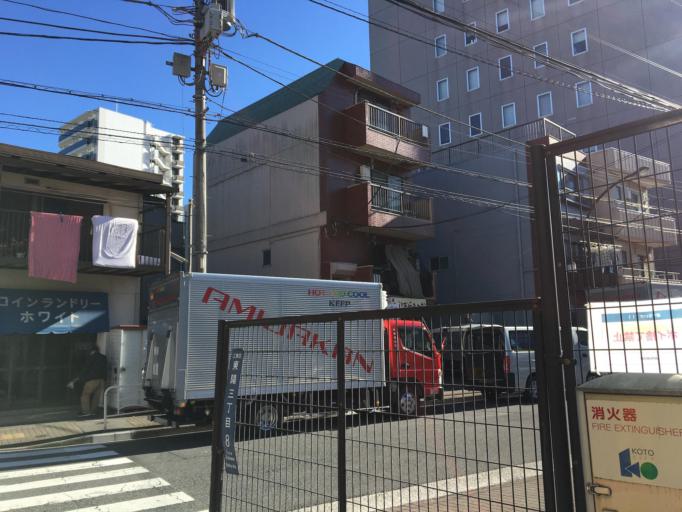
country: JP
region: Tokyo
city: Urayasu
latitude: 35.6702
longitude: 139.8092
